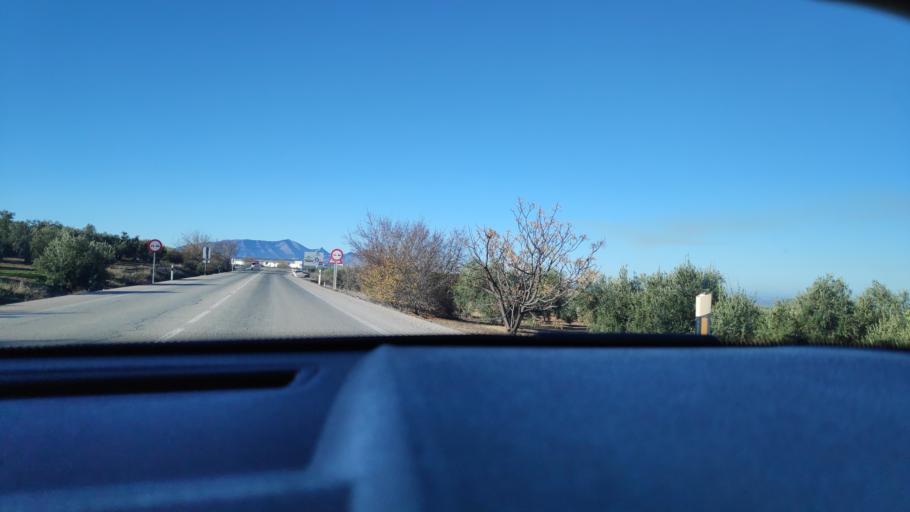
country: ES
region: Andalusia
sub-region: Provincia de Jaen
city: Mancha Real
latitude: 37.8054
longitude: -3.6231
